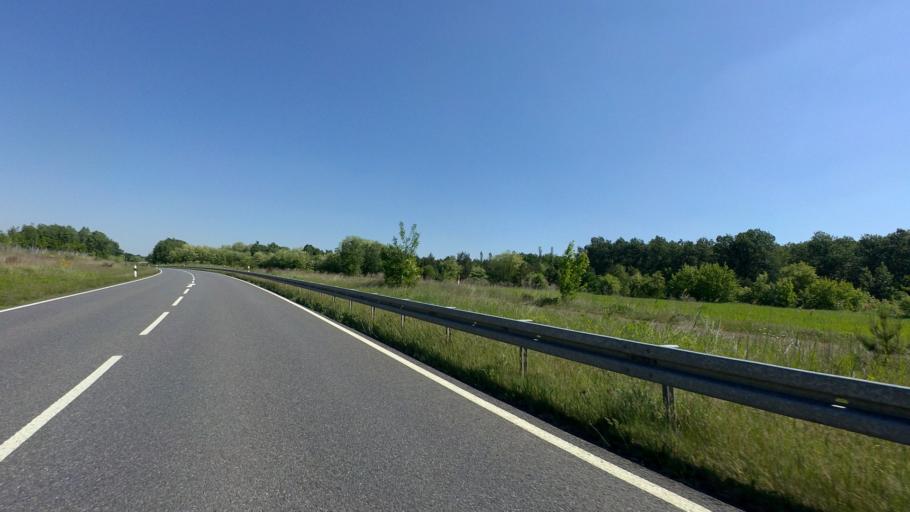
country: DE
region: Brandenburg
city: Spremberg
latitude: 51.5774
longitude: 14.3400
